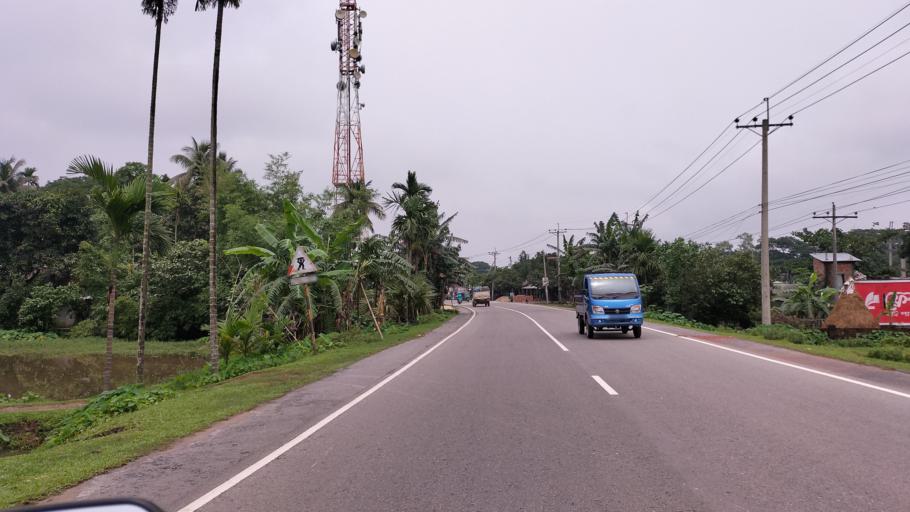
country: BD
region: Dhaka
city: Netrakona
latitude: 24.8494
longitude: 90.6427
